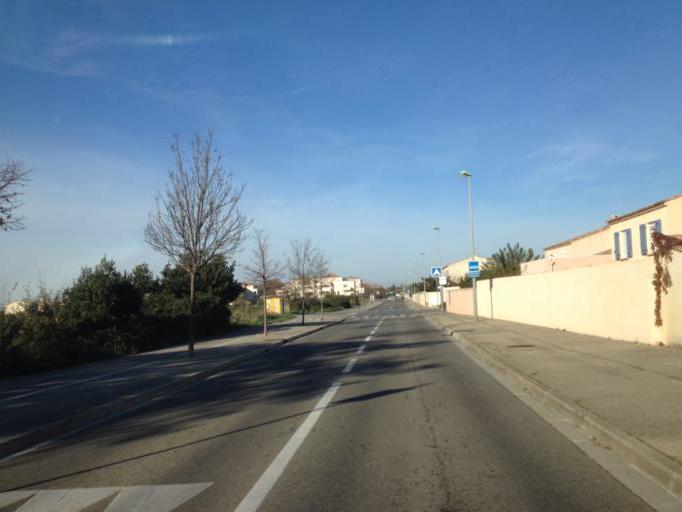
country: FR
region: Provence-Alpes-Cote d'Azur
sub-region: Departement des Bouches-du-Rhone
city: Istres
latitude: 43.5085
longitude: 4.9676
